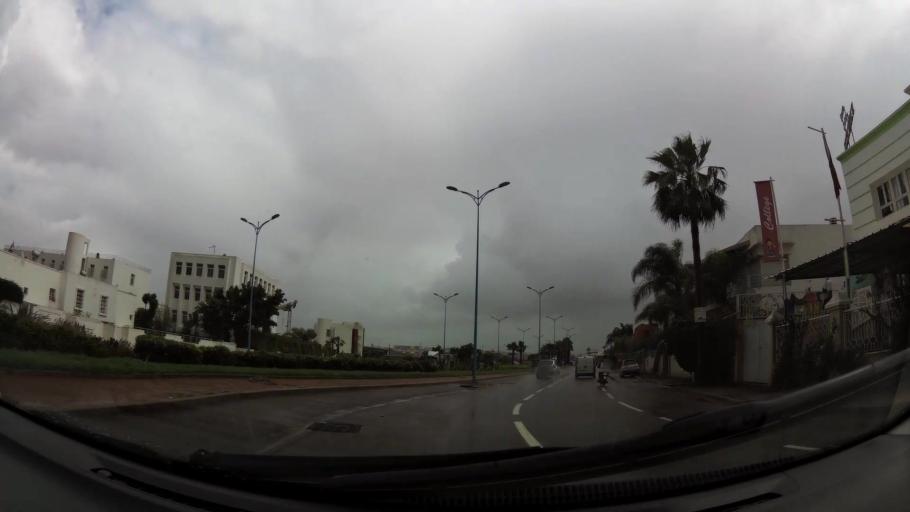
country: MA
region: Grand Casablanca
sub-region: Casablanca
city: Casablanca
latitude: 33.5394
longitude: -7.6657
